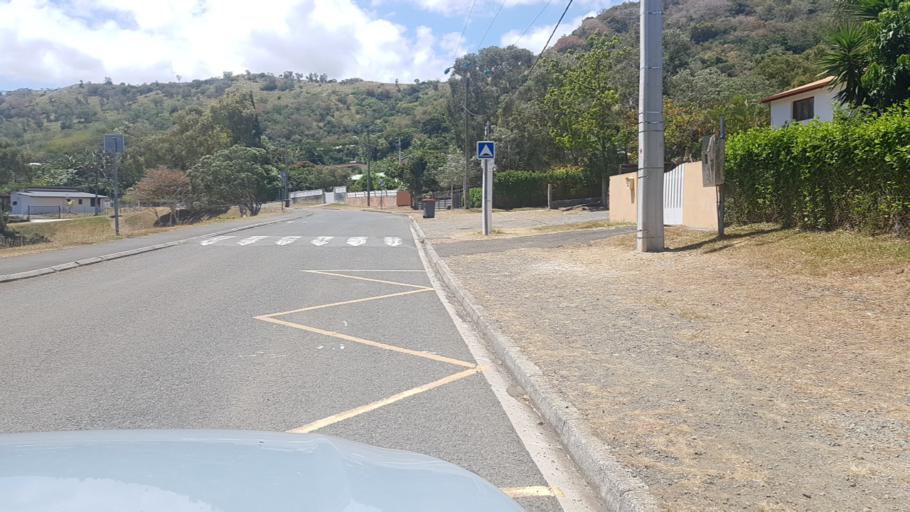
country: NC
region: South Province
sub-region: Dumbea
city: Dumbea
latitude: -22.1352
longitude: 166.4326
